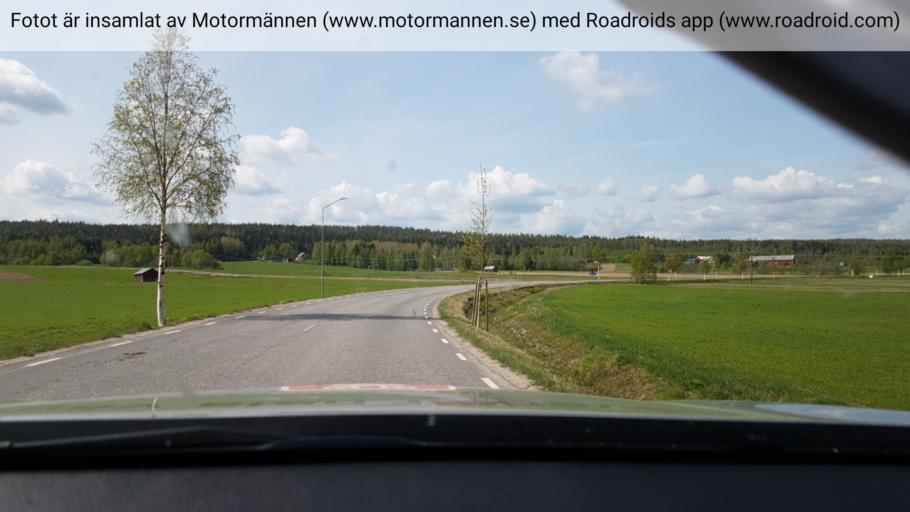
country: SE
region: Vaesterbotten
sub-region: Vannas Kommun
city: Vannasby
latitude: 63.8513
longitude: 19.9115
